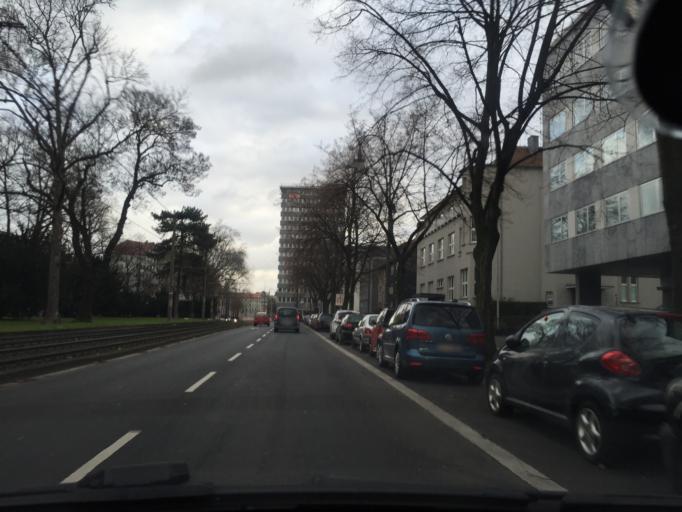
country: DE
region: North Rhine-Westphalia
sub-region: Regierungsbezirk Koln
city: Neustadt/Sued
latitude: 50.9229
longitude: 6.9542
